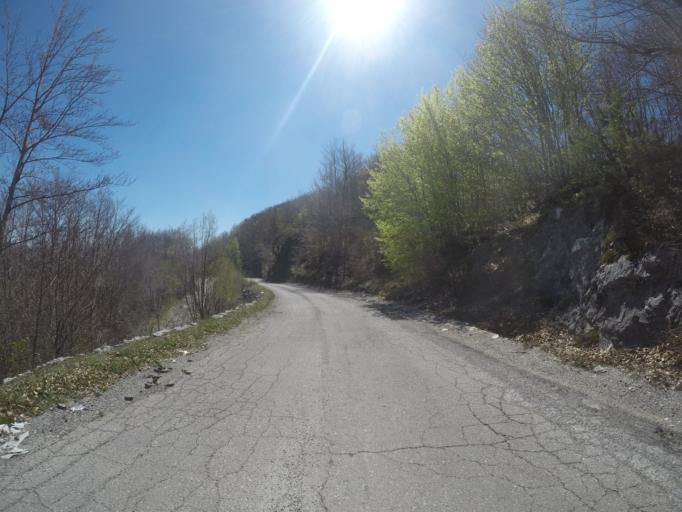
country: ME
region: Cetinje
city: Cetinje
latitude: 42.4346
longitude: 18.8668
